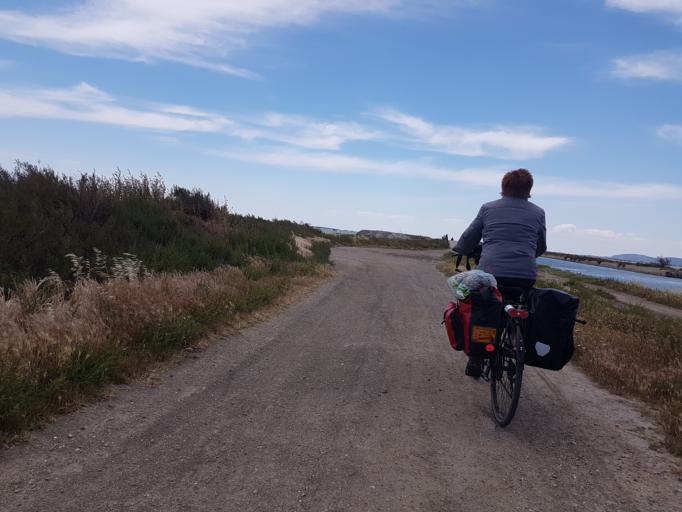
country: FR
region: Languedoc-Roussillon
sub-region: Departement de l'Herault
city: Villeneuve-les-Maguelone
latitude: 43.5092
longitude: 3.8705
